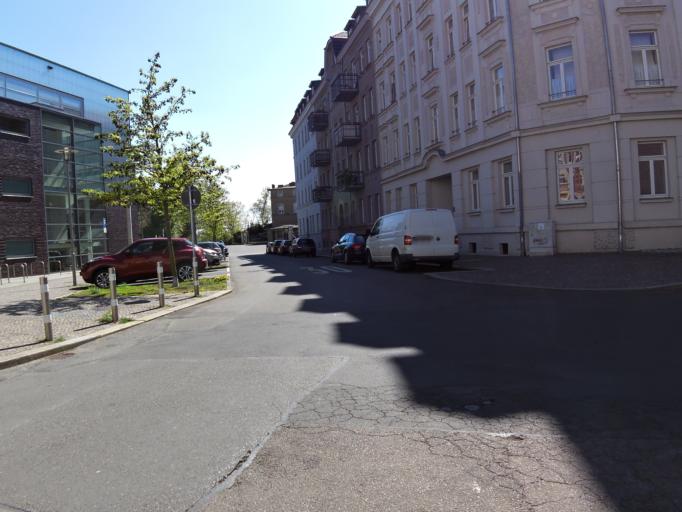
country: DE
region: Saxony
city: Leipzig
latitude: 51.3685
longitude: 12.3408
